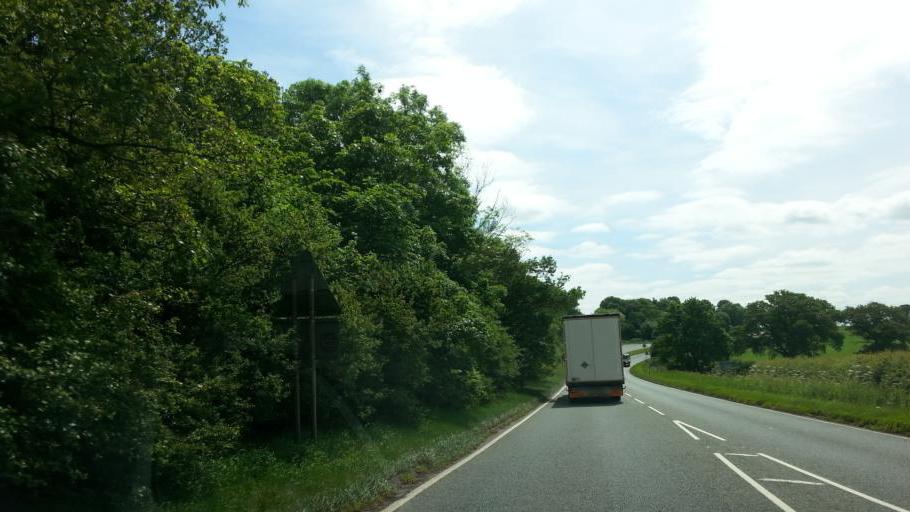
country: GB
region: England
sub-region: Nottinghamshire
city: Cotgrave
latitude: 52.8575
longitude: -1.0372
